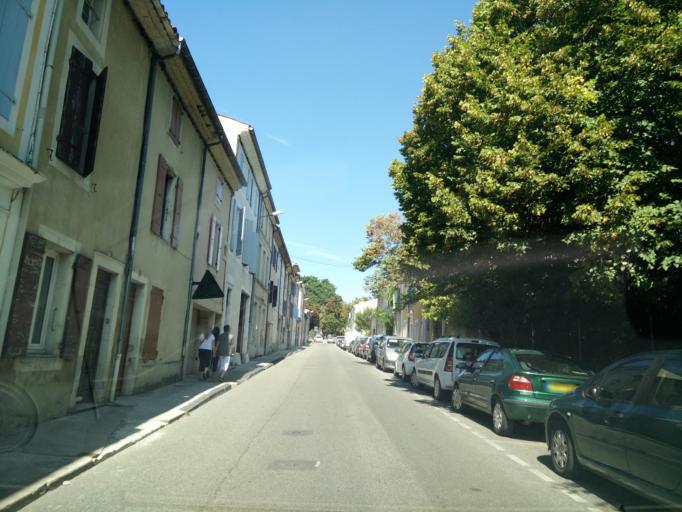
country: FR
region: Rhone-Alpes
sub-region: Departement de la Drome
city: Dieulefit
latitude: 44.5236
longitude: 5.0627
